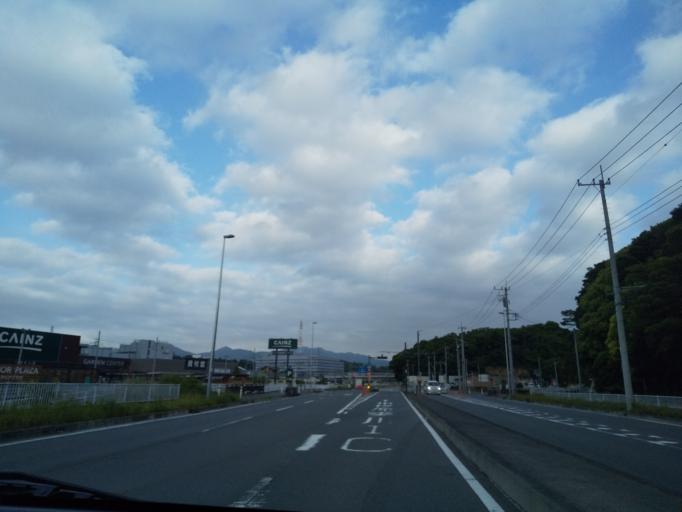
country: JP
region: Kanagawa
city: Zama
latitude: 35.5268
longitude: 139.3675
